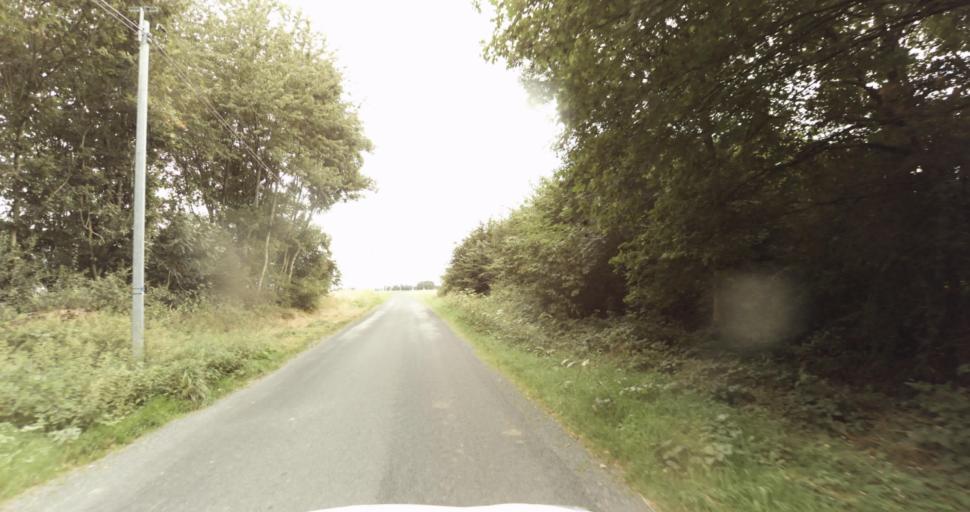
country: FR
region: Haute-Normandie
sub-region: Departement de l'Eure
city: La Madeleine-de-Nonancourt
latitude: 48.8564
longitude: 1.2270
